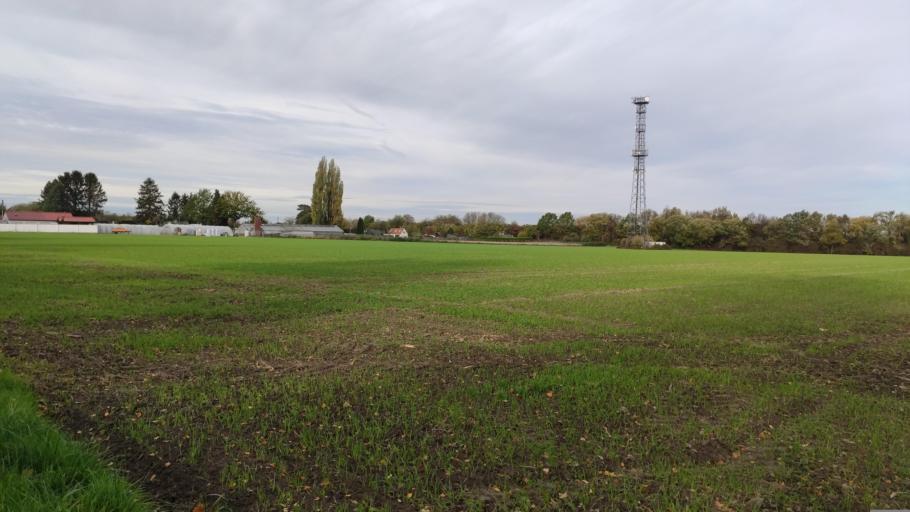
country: DE
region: North Rhine-Westphalia
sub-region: Regierungsbezirk Munster
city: Recklinghausen
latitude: 51.6314
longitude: 7.2033
